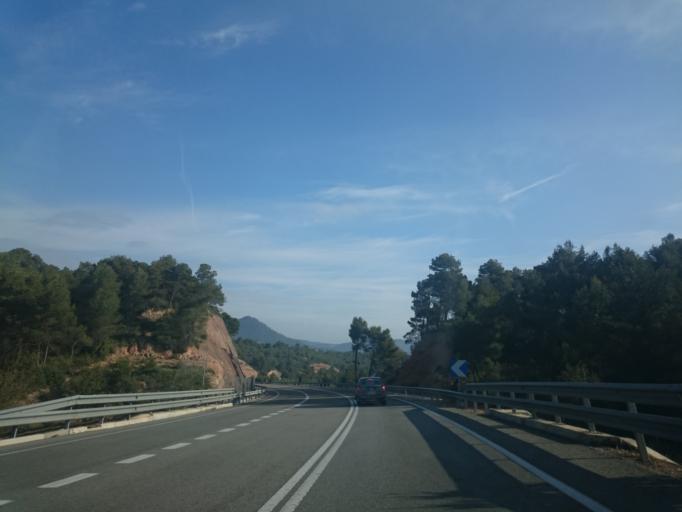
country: ES
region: Catalonia
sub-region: Provincia de Barcelona
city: Castellfollit del Boix
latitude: 41.6488
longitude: 1.7077
